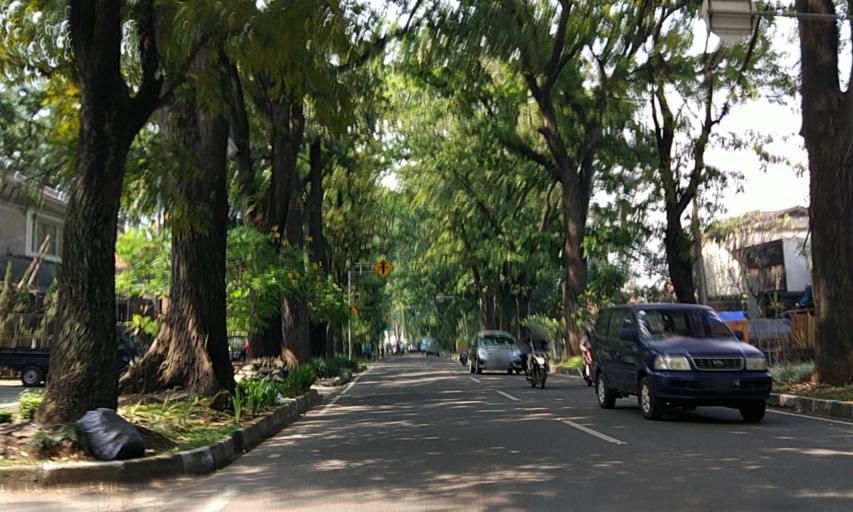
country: ID
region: West Java
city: Bandung
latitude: -6.9014
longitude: 107.5988
